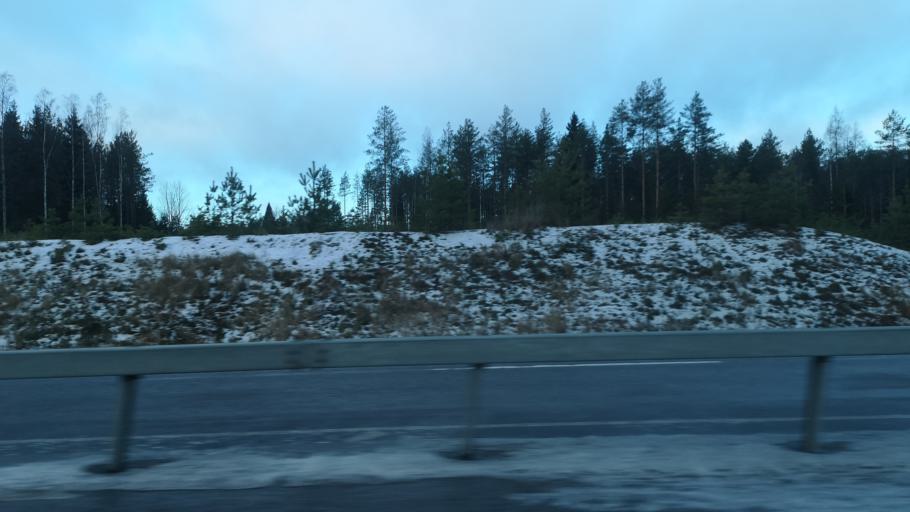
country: FI
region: Southern Savonia
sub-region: Mikkeli
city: Maentyharju
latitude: 61.4871
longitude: 26.7698
